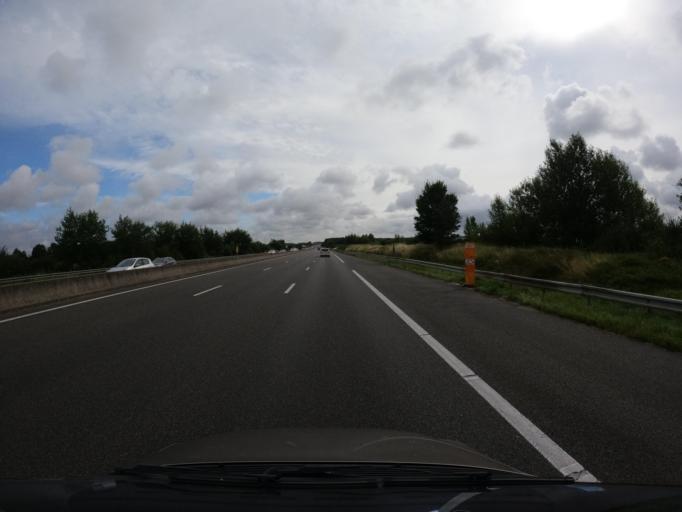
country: FR
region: Centre
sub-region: Departement du Loir-et-Cher
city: Herbault
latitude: 47.5895
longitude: 1.0860
